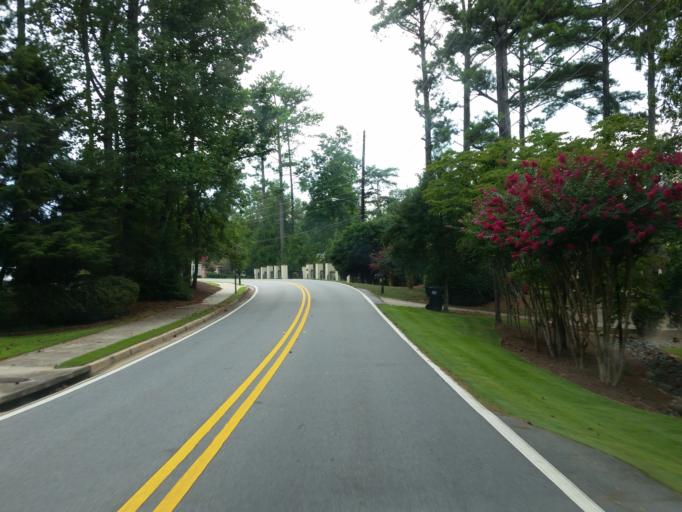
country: US
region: Georgia
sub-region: Fulton County
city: Sandy Springs
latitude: 33.9506
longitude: -84.4260
